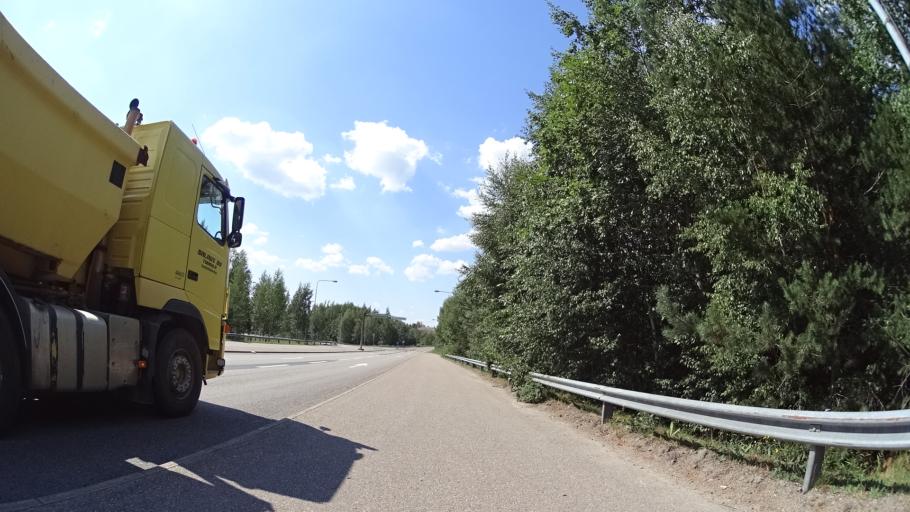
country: FI
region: Uusimaa
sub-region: Helsinki
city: Vantaa
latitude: 60.3410
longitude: 25.0000
